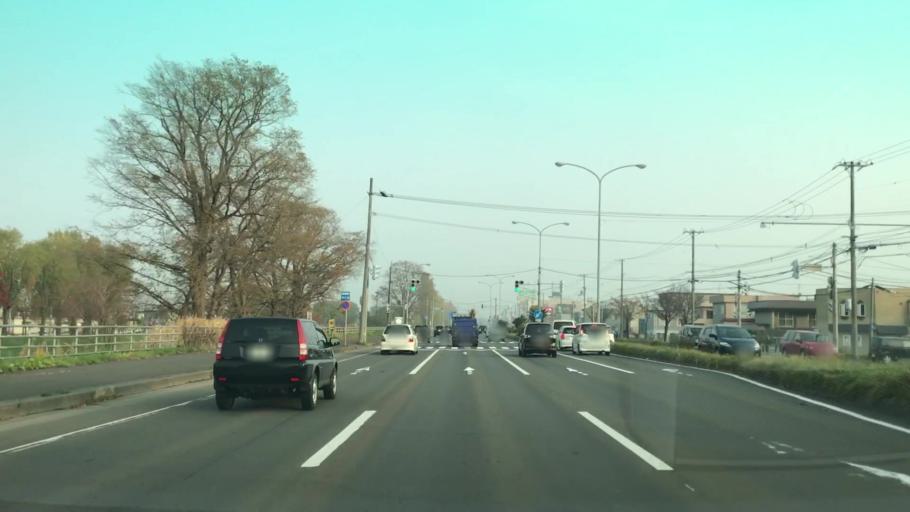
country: JP
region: Hokkaido
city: Ishikari
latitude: 43.1532
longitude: 141.3516
